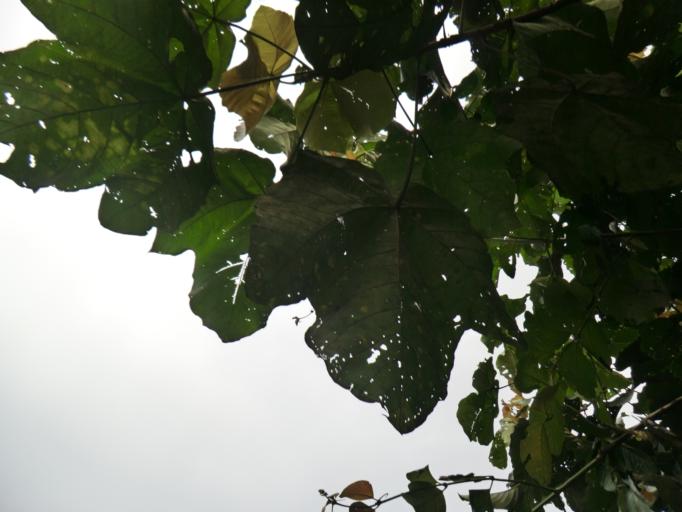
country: MY
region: Sarawak
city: Simanggang
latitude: 1.0358
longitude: 112.0461
